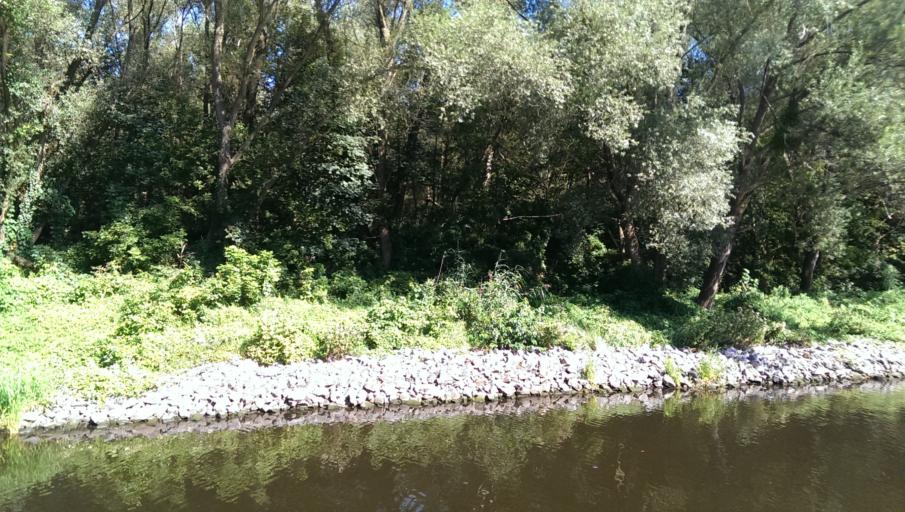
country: DE
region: Berlin
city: Wannsee
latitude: 52.3971
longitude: 13.1658
